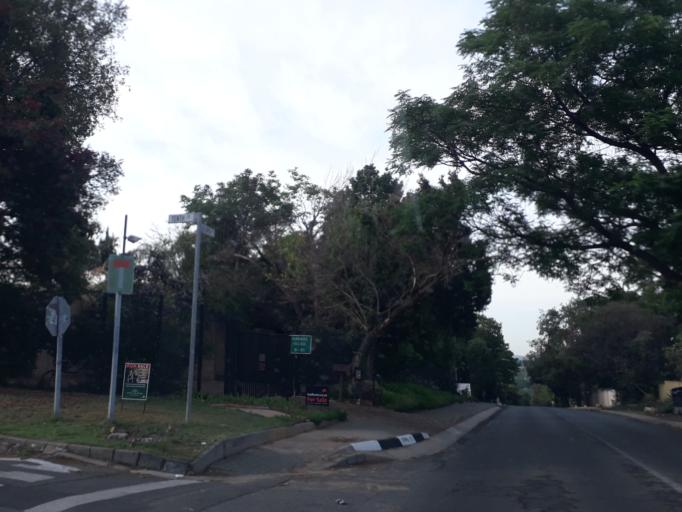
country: ZA
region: Gauteng
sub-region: City of Johannesburg Metropolitan Municipality
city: Johannesburg
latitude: -26.0936
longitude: 28.0353
